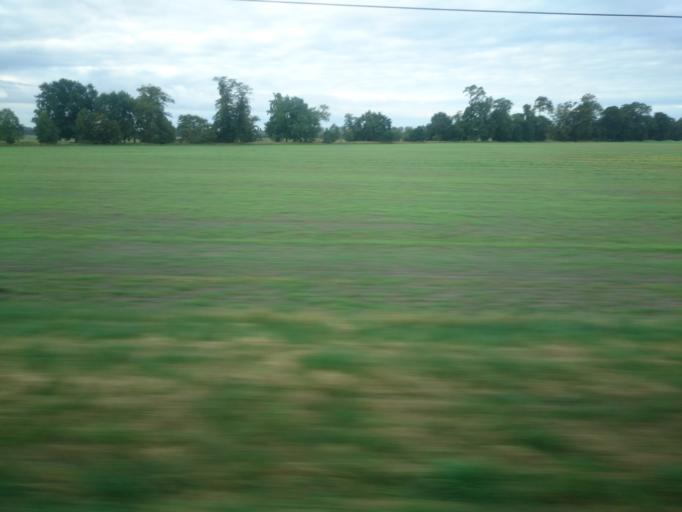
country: DE
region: Mecklenburg-Vorpommern
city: Ferdinandshof
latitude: 53.7059
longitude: 13.8526
